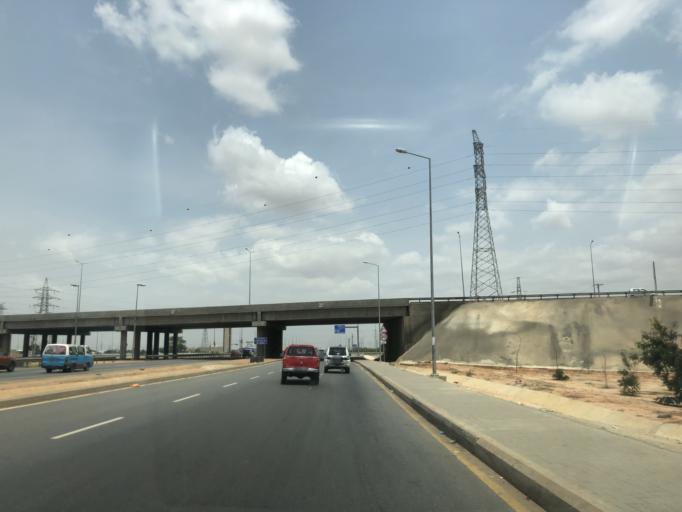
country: AO
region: Luanda
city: Luanda
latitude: -8.9737
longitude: 13.2529
